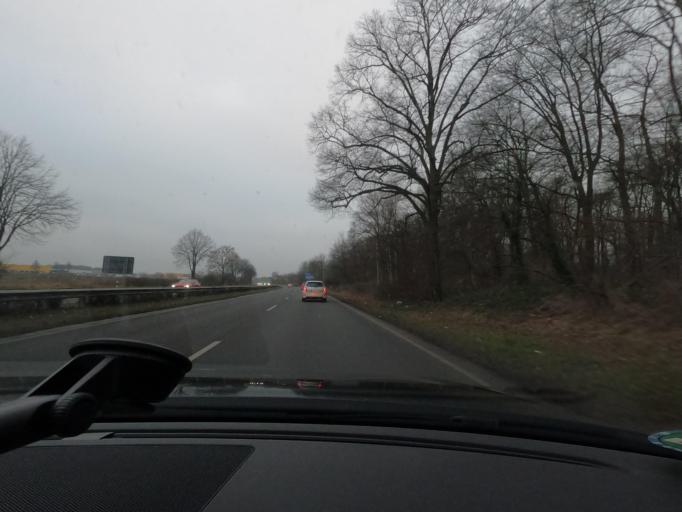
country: DE
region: North Rhine-Westphalia
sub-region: Regierungsbezirk Dusseldorf
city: Willich
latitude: 51.2969
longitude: 6.5285
